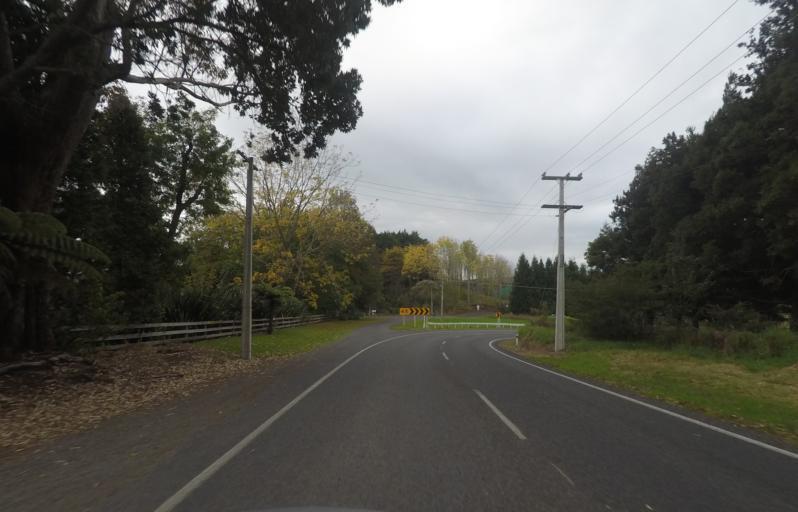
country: NZ
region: Bay of Plenty
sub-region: Western Bay of Plenty District
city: Waihi Beach
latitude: -37.4400
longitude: 175.9456
